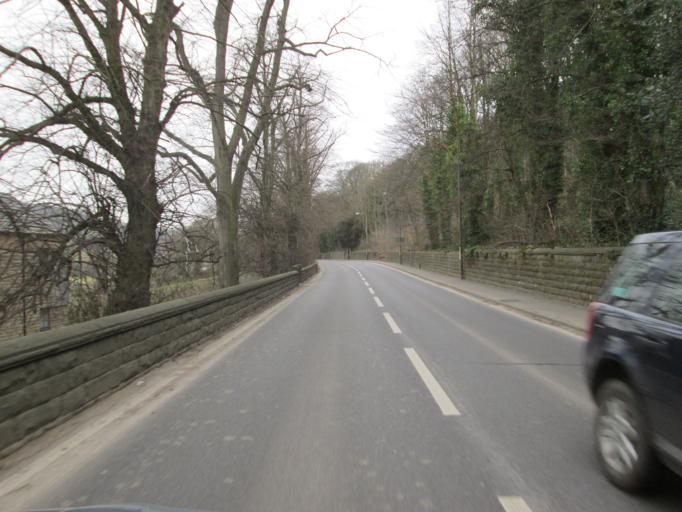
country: GB
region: England
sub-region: Derbyshire
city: Matlock
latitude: 53.1687
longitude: -1.6028
